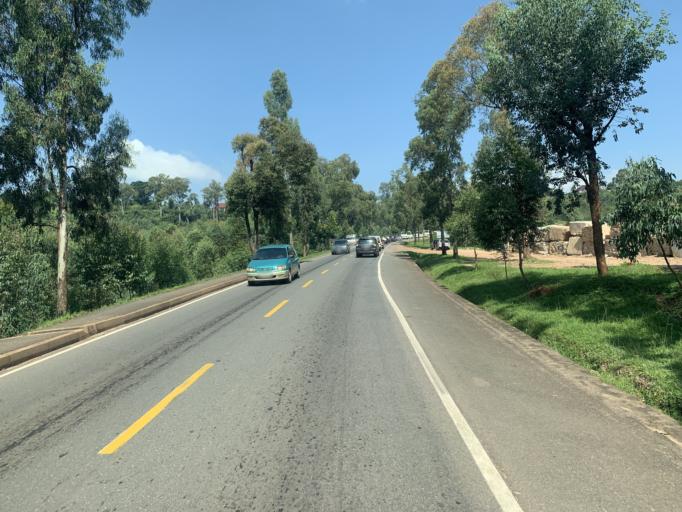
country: RW
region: Kigali
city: Kigali
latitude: -1.9925
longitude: 29.9210
